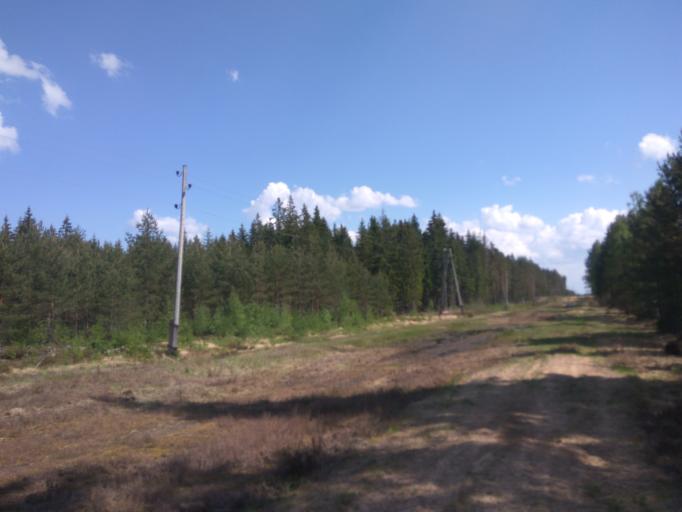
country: LV
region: Kuldigas Rajons
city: Kuldiga
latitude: 57.1847
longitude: 21.9940
